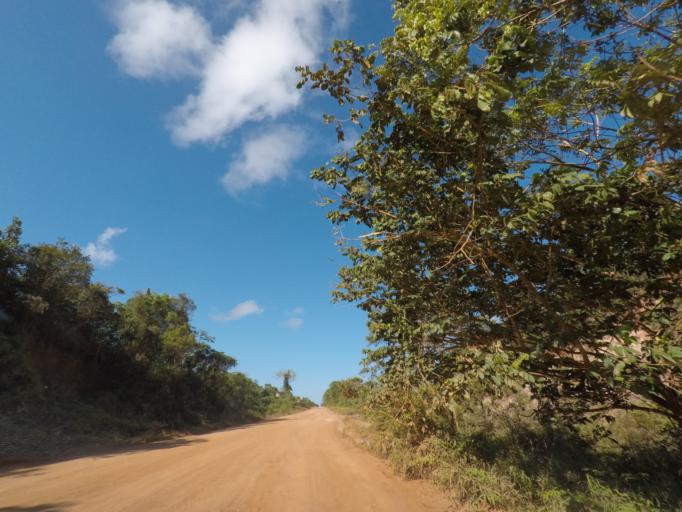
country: BR
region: Bahia
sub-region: Marau
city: Marau
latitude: -14.1327
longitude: -38.9959
